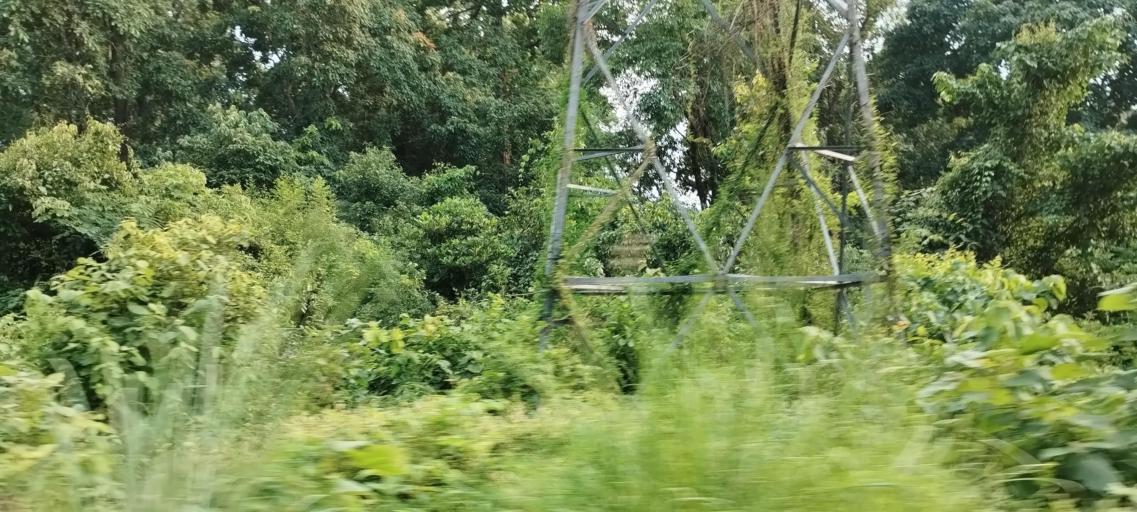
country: NP
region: Mid Western
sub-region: Bheri Zone
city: Bardiya
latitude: 28.4299
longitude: 81.3481
